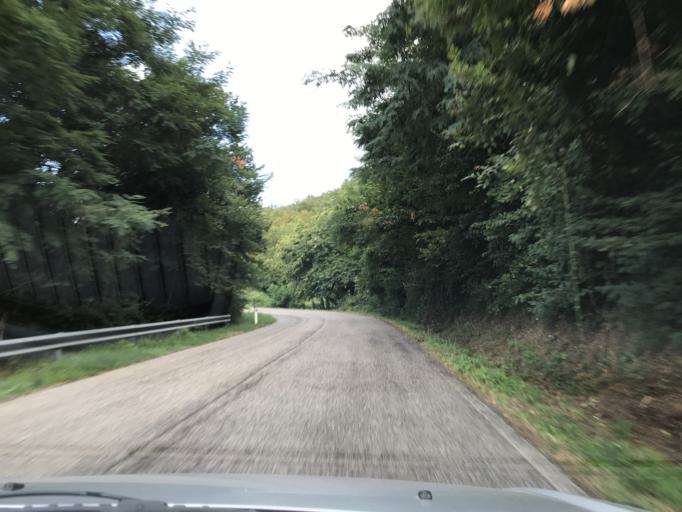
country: IT
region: Umbria
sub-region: Provincia di Terni
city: Guardea
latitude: 42.6556
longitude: 12.3427
